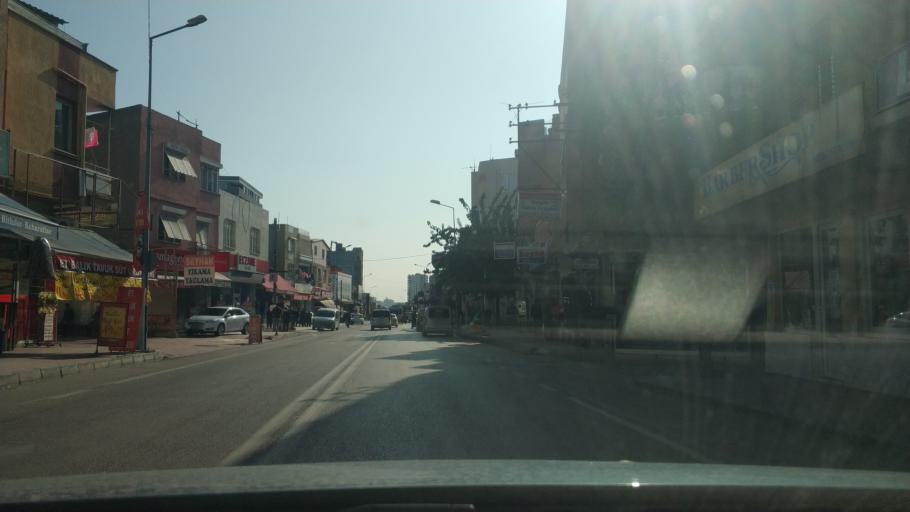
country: TR
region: Adana
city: Seyhan
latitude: 37.0175
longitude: 35.2990
